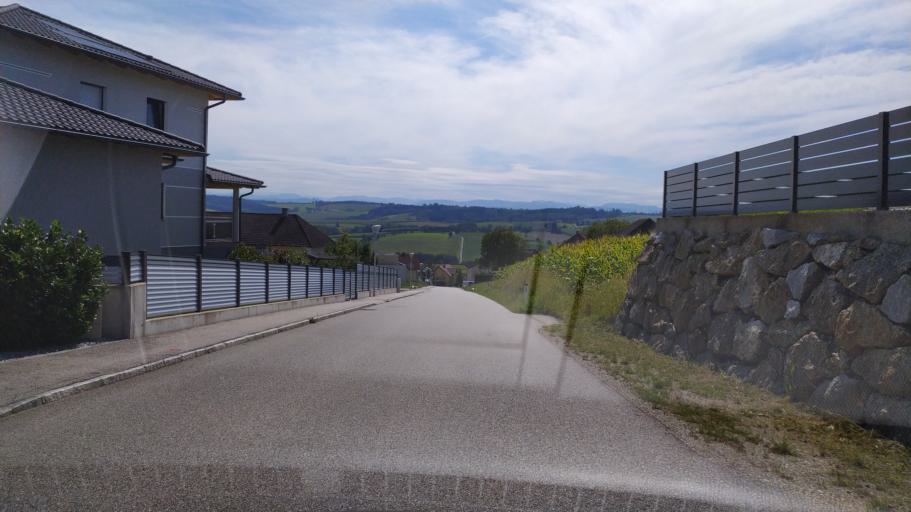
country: AT
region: Lower Austria
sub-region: Politischer Bezirk Amstetten
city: Strengberg
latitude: 48.1428
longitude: 14.6448
